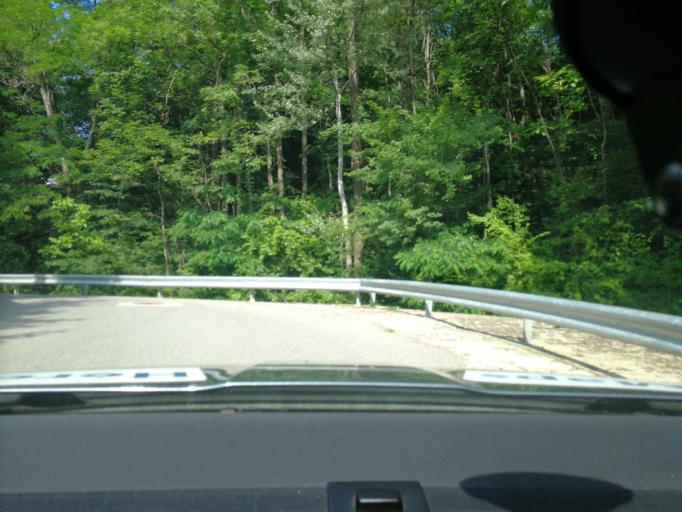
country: RO
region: Prahova
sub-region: Comuna Cornu
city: Cornu de Jos
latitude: 45.1431
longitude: 25.7071
